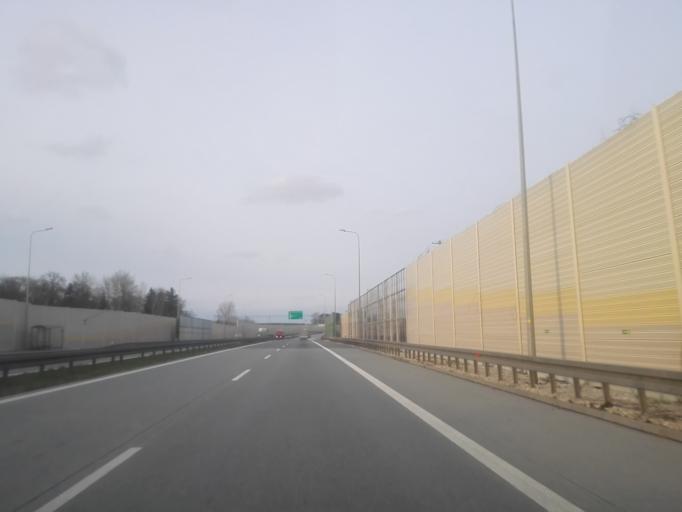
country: PL
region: Lodz Voivodeship
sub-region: Powiat skierniewicki
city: Kowiesy
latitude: 51.8381
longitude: 20.3460
